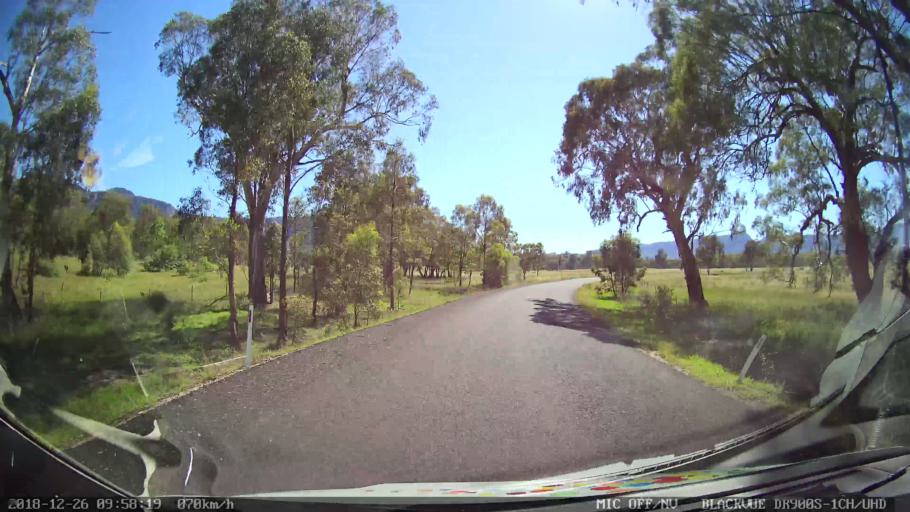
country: AU
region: New South Wales
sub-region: Mid-Western Regional
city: Kandos
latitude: -33.0387
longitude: 150.2035
